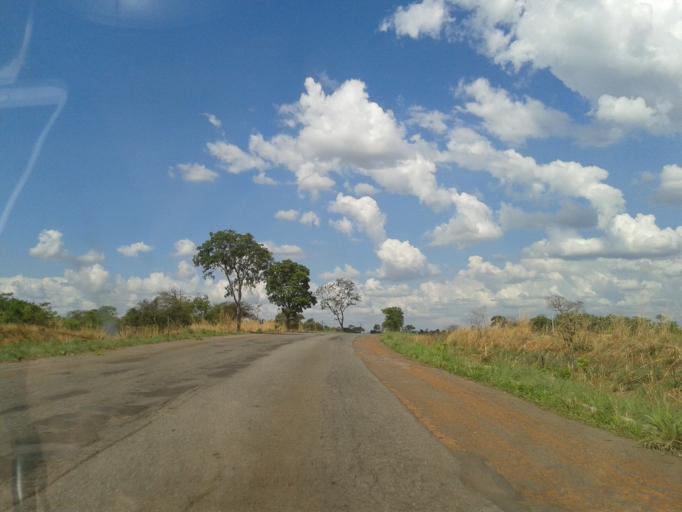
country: BR
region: Goias
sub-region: Caldas Novas
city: Caldas Novas
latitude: -17.6996
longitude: -48.7247
